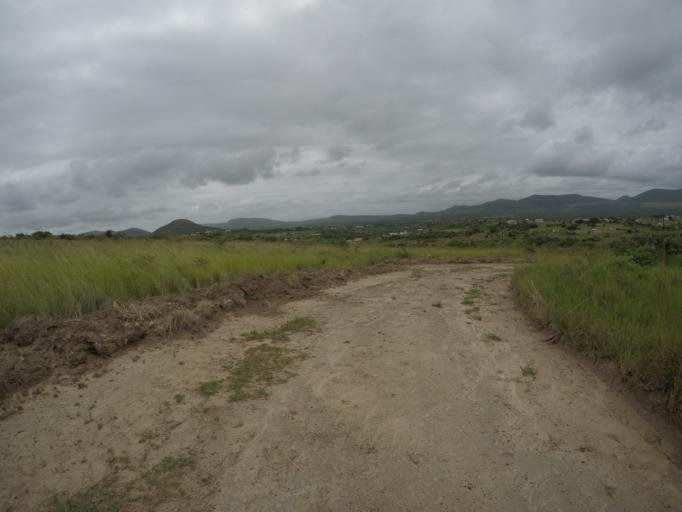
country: ZA
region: KwaZulu-Natal
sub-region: uThungulu District Municipality
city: Empangeni
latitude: -28.6055
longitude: 31.8353
